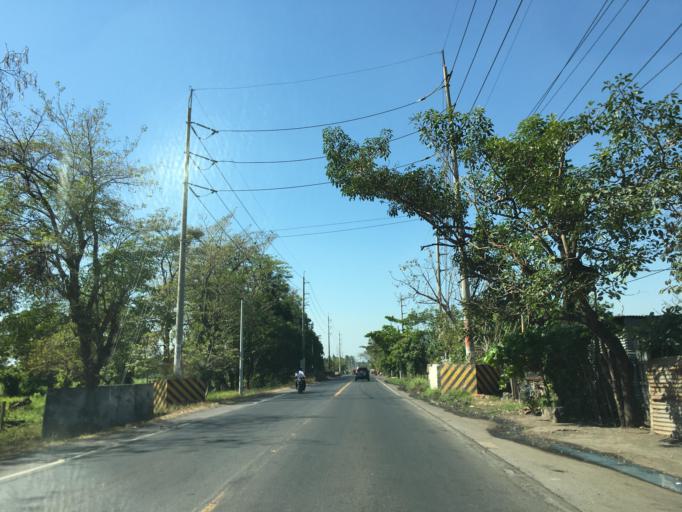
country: GT
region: Escuintla
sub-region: Municipio de Masagua
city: Masagua
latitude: 14.2134
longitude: -90.8369
